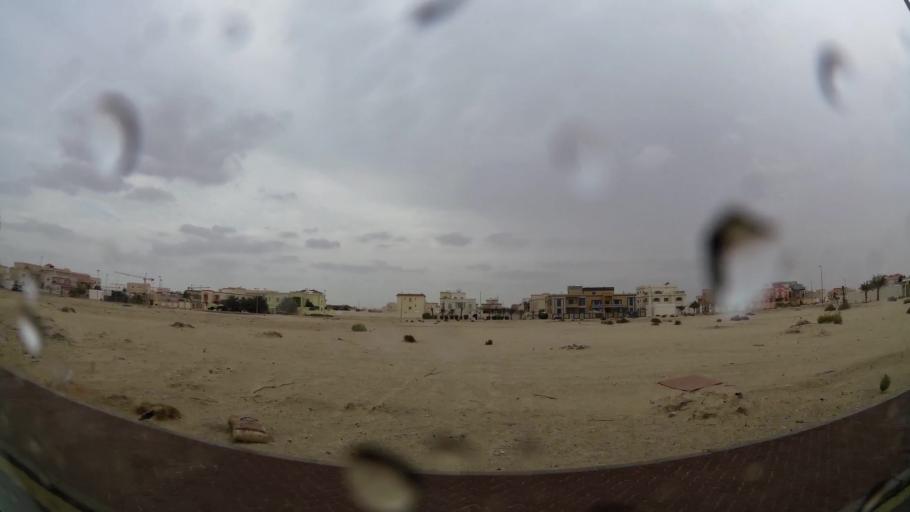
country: AE
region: Abu Dhabi
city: Abu Dhabi
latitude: 24.3651
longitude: 54.6395
